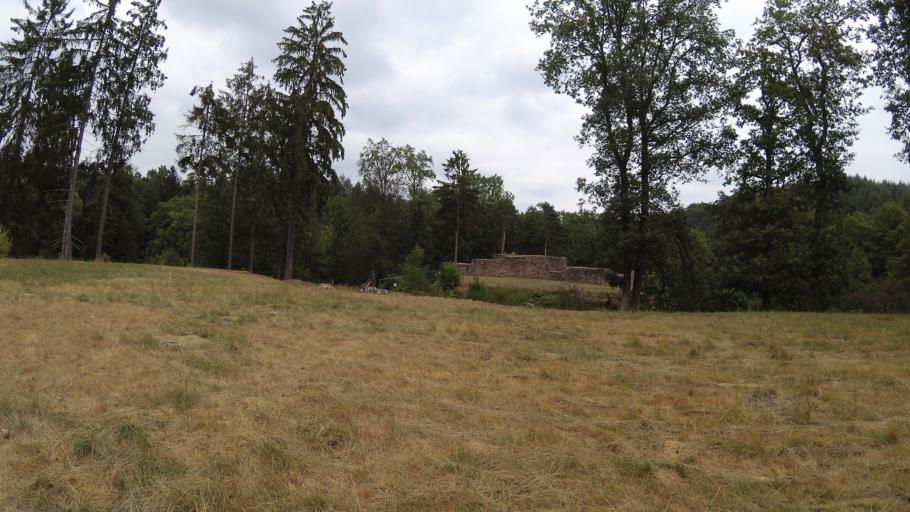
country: DE
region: Saarland
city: Homburg
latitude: 49.3122
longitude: 7.3754
